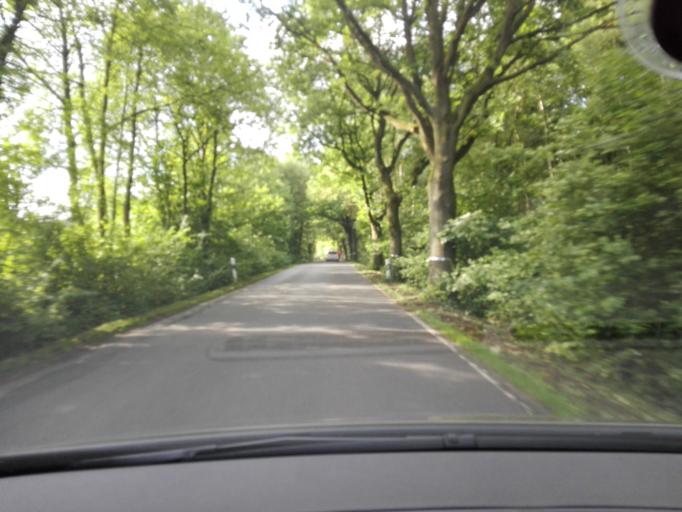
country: DE
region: North Rhine-Westphalia
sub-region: Regierungsbezirk Arnsberg
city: Frondenberg
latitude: 51.4912
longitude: 7.7546
